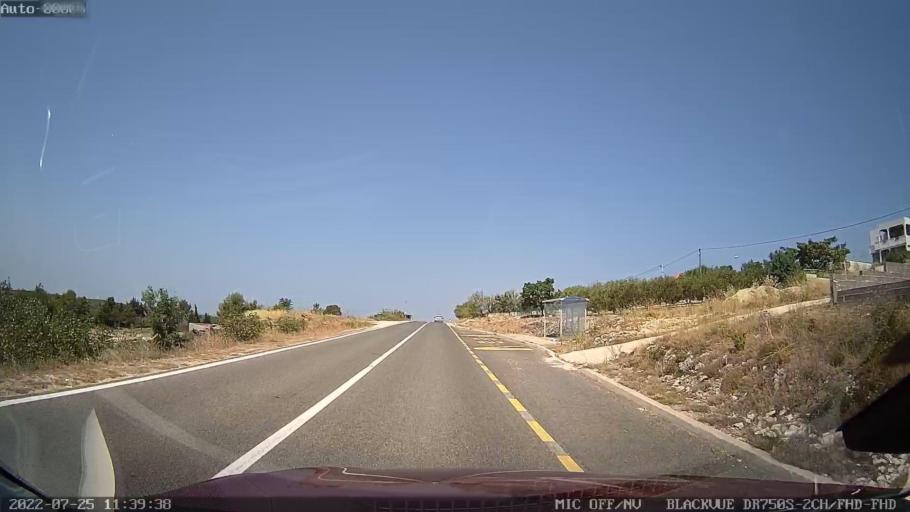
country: HR
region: Zadarska
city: Razanac
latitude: 44.2581
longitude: 15.3694
